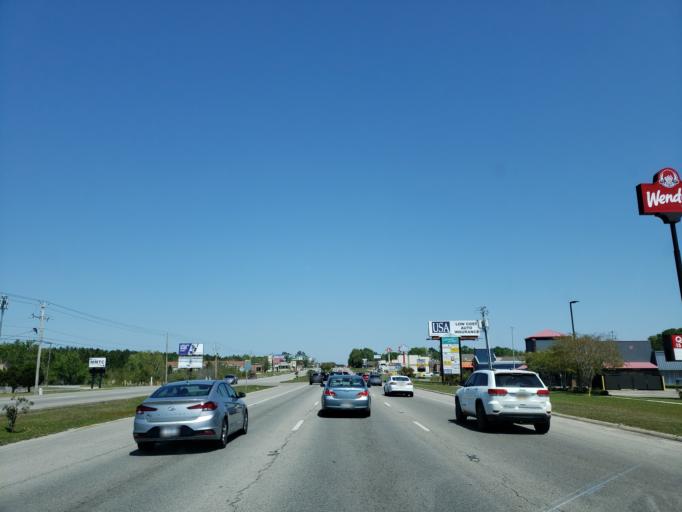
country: US
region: Mississippi
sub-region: Harrison County
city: Lyman
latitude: 30.4593
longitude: -89.1008
